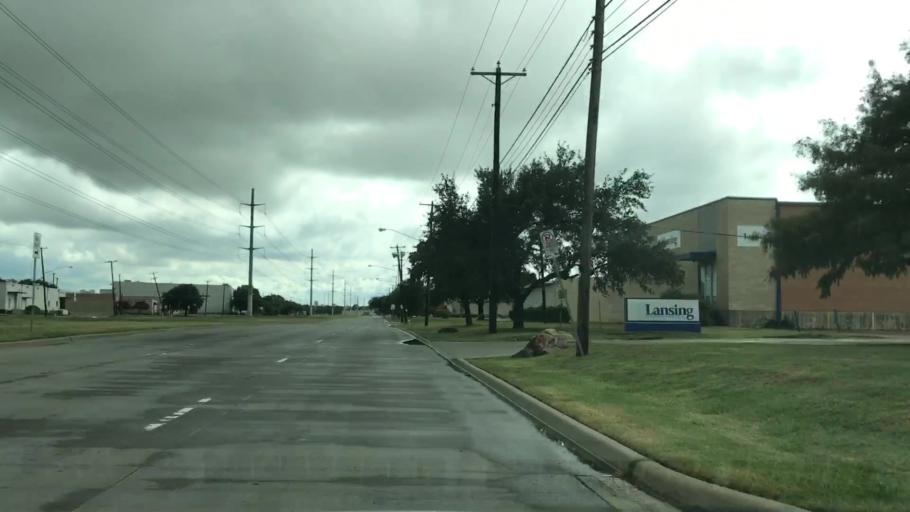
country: US
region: Texas
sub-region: Dallas County
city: Irving
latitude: 32.8241
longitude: -96.8905
